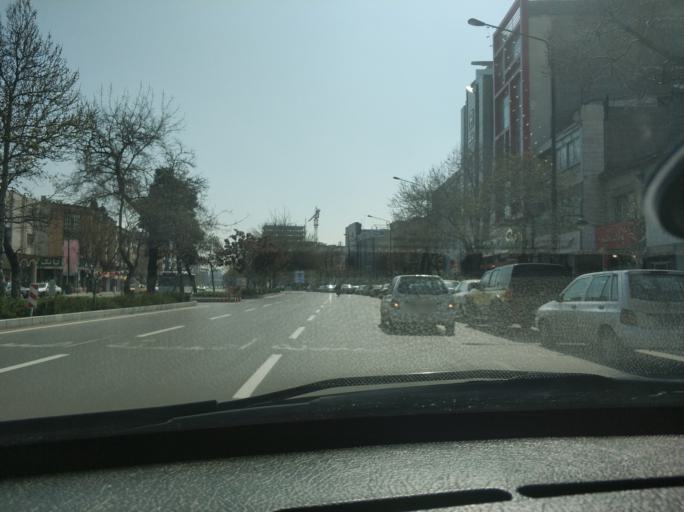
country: IR
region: Razavi Khorasan
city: Mashhad
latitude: 36.2953
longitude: 59.5762
